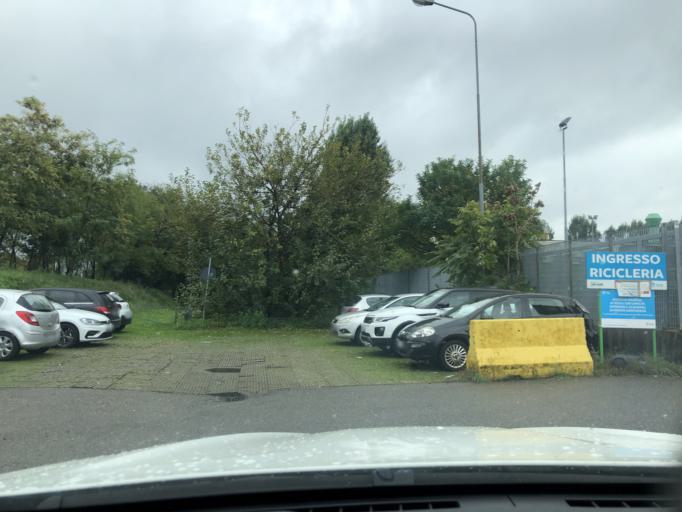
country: IT
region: Lombardy
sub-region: Citta metropolitana di Milano
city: Settimo Milanese
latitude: 45.4607
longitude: 9.0674
